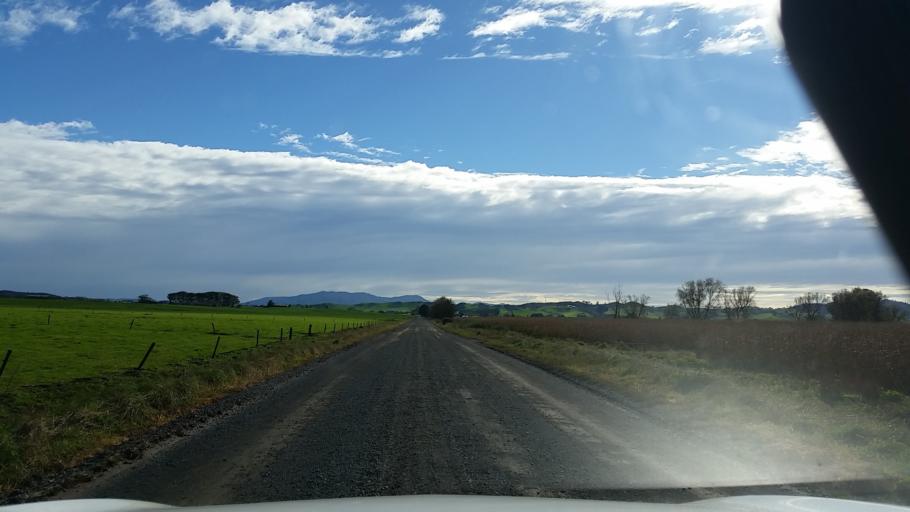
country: NZ
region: Waikato
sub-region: Hamilton City
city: Hamilton
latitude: -37.6321
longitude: 175.4287
